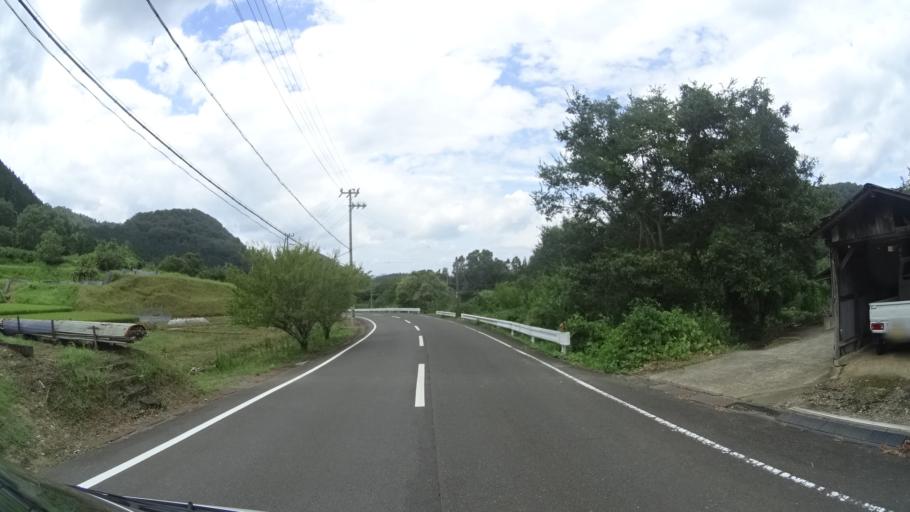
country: JP
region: Kyoto
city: Ayabe
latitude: 35.2884
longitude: 135.2754
